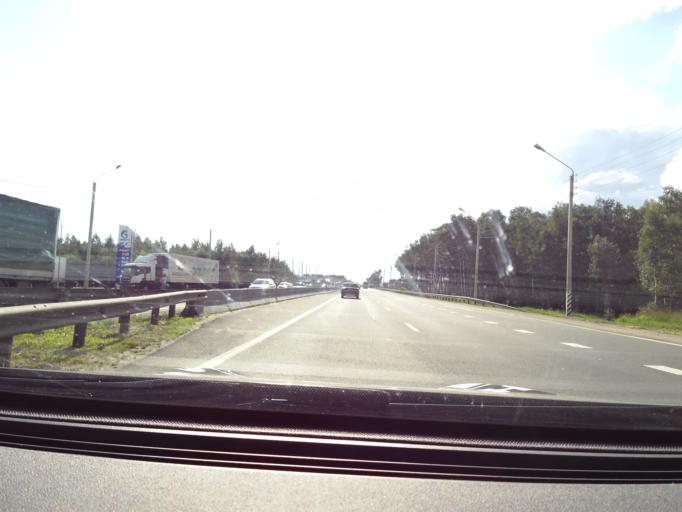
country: RU
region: Nizjnij Novgorod
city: Gorbatovka
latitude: 56.3067
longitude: 43.6845
